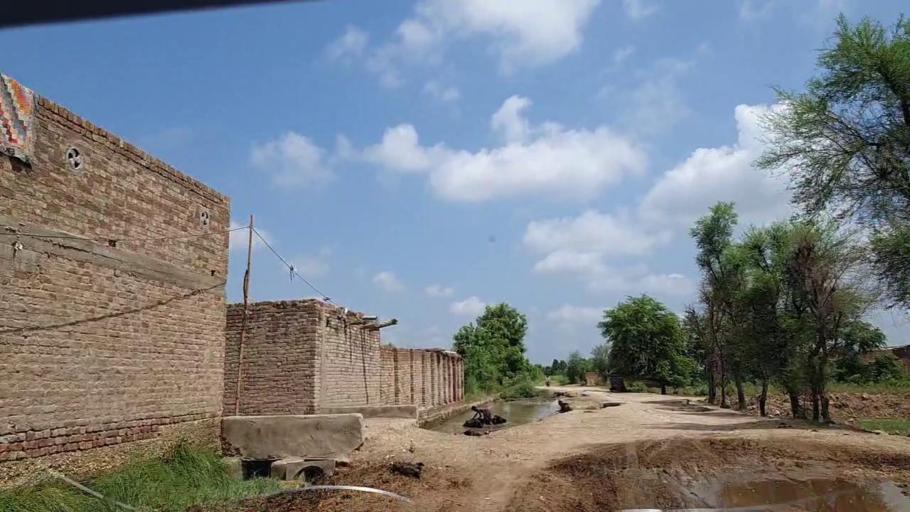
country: PK
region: Sindh
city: Tharu Shah
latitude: 26.8992
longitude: 68.0396
